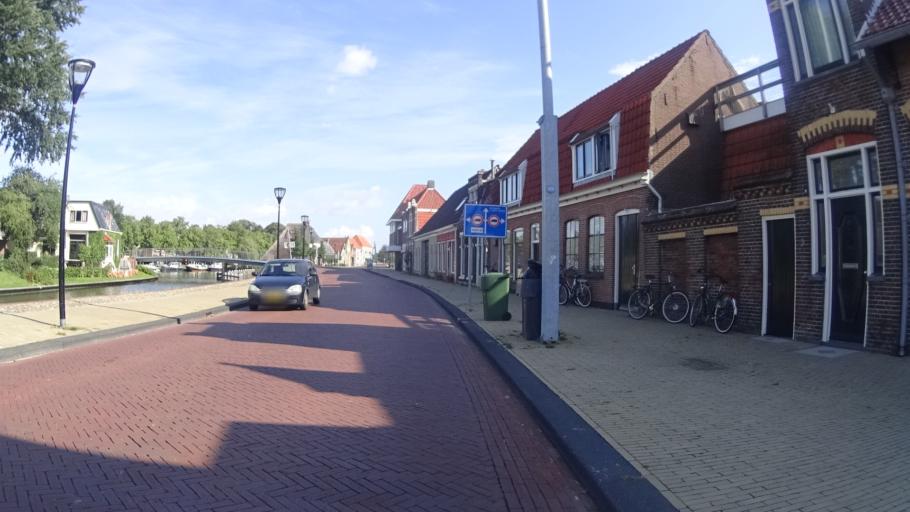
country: NL
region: Friesland
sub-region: Gemeente Franekeradeel
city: Franeker
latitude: 53.1846
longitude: 5.5487
